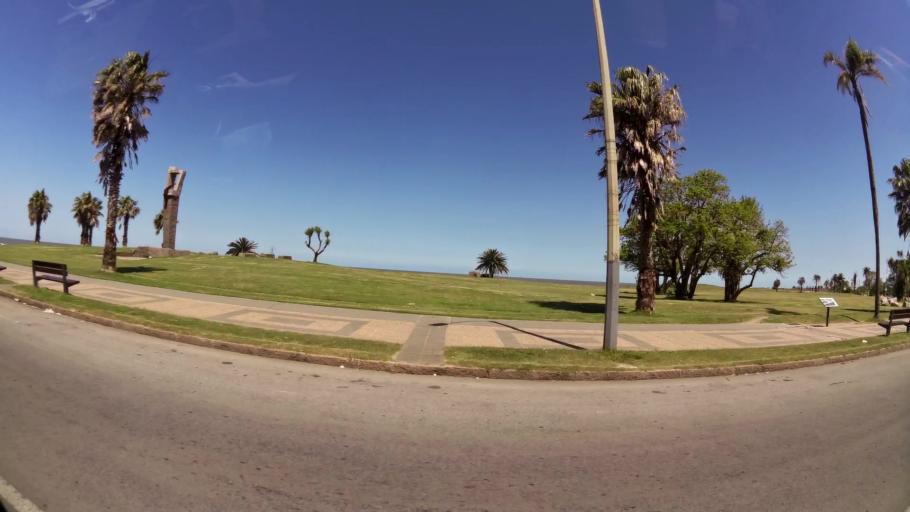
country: UY
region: Montevideo
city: Montevideo
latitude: -34.9284
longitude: -56.1593
